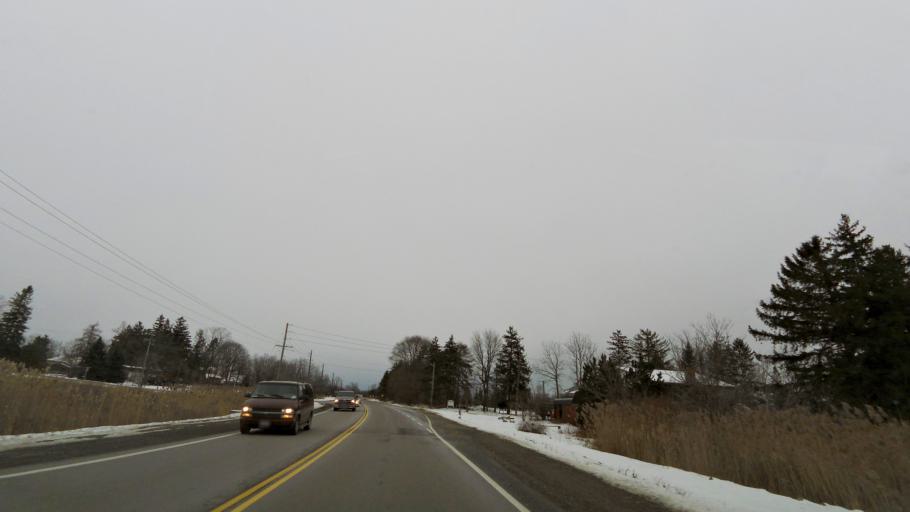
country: CA
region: Ontario
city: Ancaster
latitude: 43.2852
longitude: -80.0395
